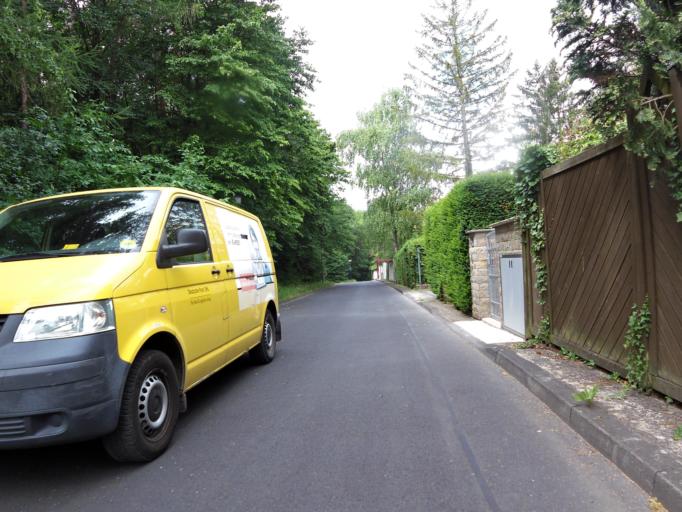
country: DE
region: Bavaria
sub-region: Regierungsbezirk Unterfranken
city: Reichenberg
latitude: 49.7669
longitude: 9.9206
